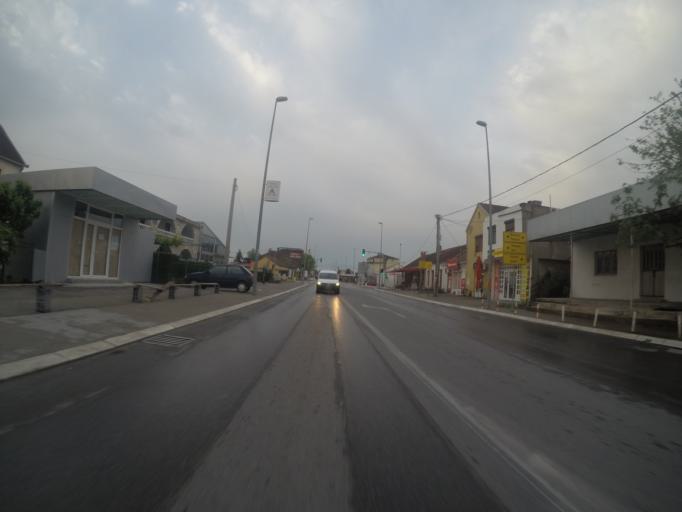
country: ME
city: Mojanovici
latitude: 42.3324
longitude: 19.2207
